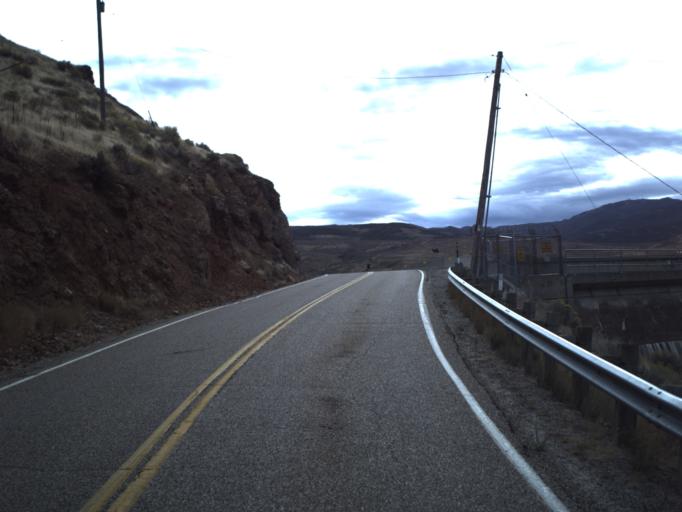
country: US
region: Utah
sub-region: Morgan County
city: Morgan
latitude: 40.9213
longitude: -111.6017
